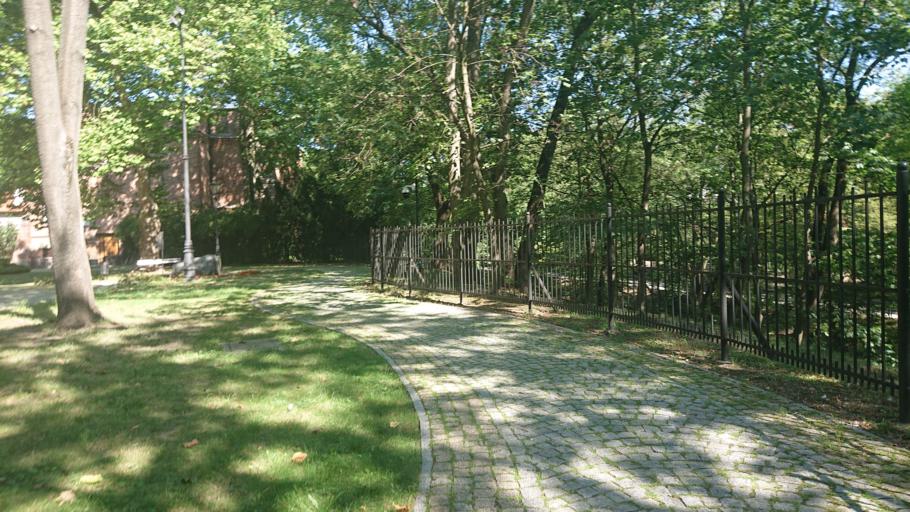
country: PL
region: Masovian Voivodeship
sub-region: Plock
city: Plock
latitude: 52.5409
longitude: 19.6903
